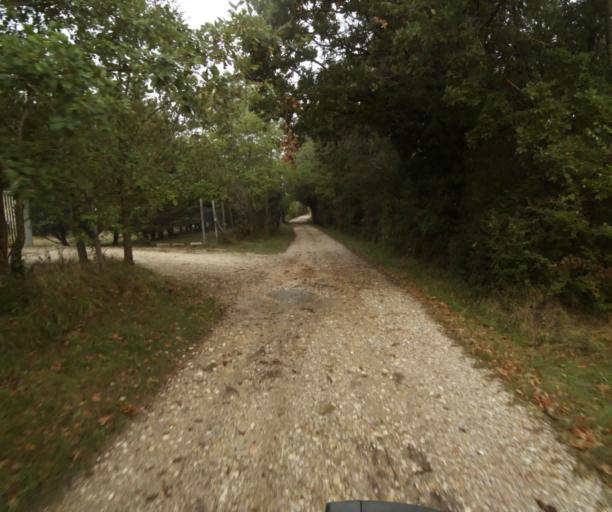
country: FR
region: Midi-Pyrenees
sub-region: Departement du Tarn-et-Garonne
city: Saint-Nauphary
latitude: 43.9354
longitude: 1.4606
